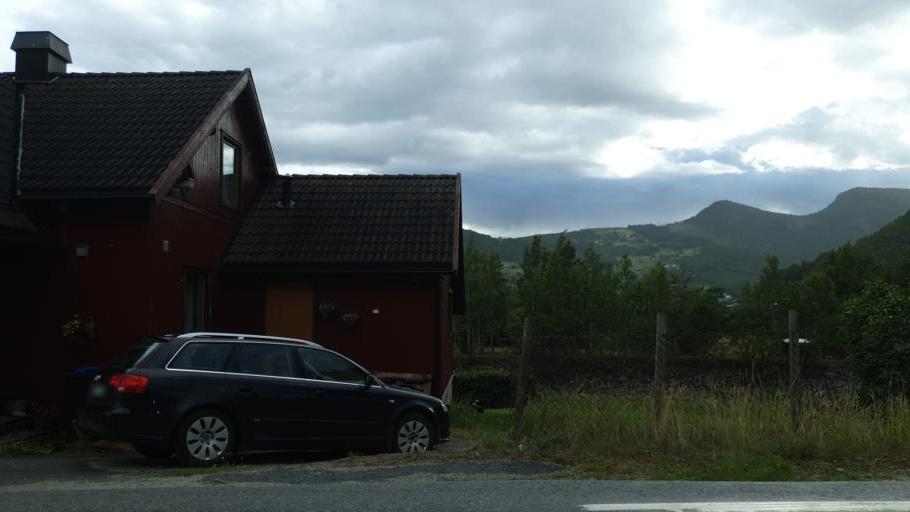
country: NO
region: Oppland
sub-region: Sel
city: Otta
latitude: 61.8494
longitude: 9.4265
